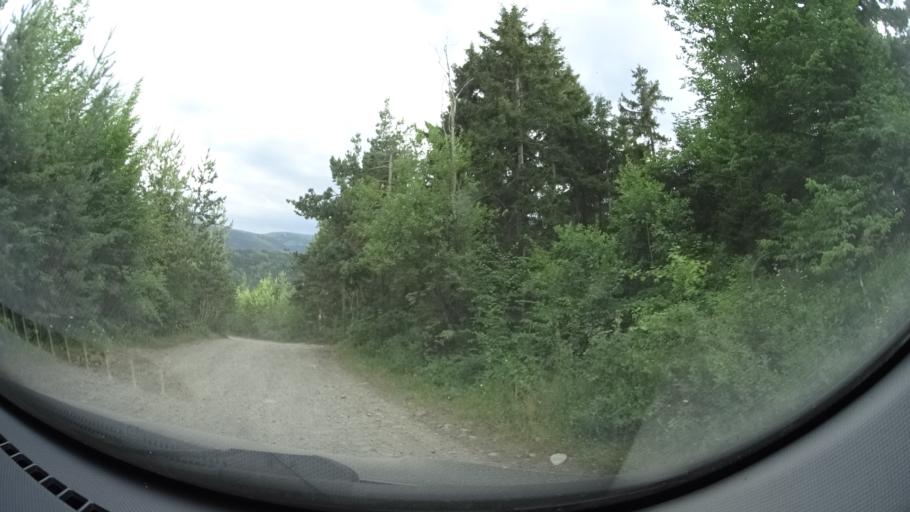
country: GE
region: Samtskhe-Javakheti
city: Adigeni
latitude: 41.6649
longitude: 42.6117
